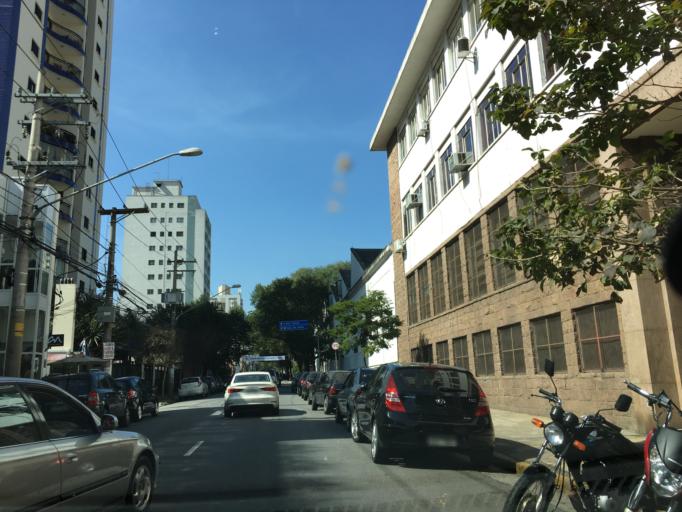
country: BR
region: Sao Paulo
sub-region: Sao Paulo
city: Sao Paulo
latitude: -23.5282
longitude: -46.6966
